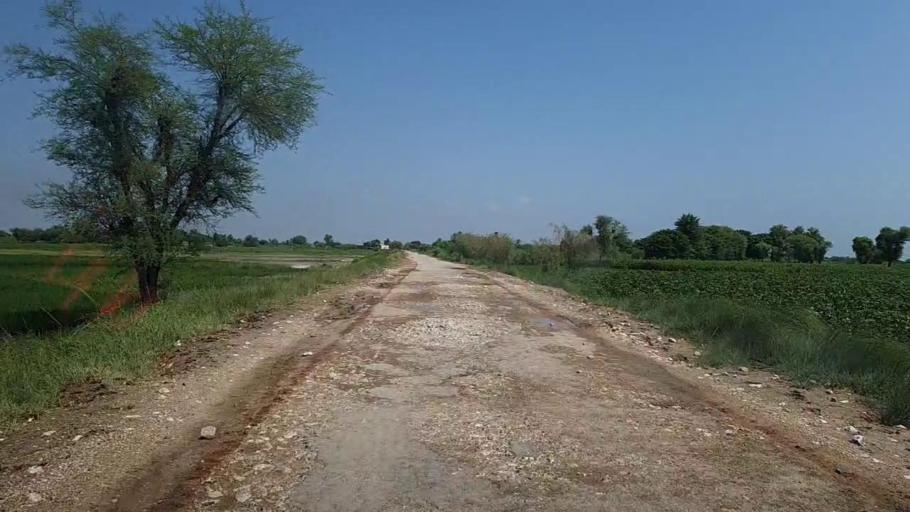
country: PK
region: Sindh
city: Bhiria
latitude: 26.8905
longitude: 68.2281
